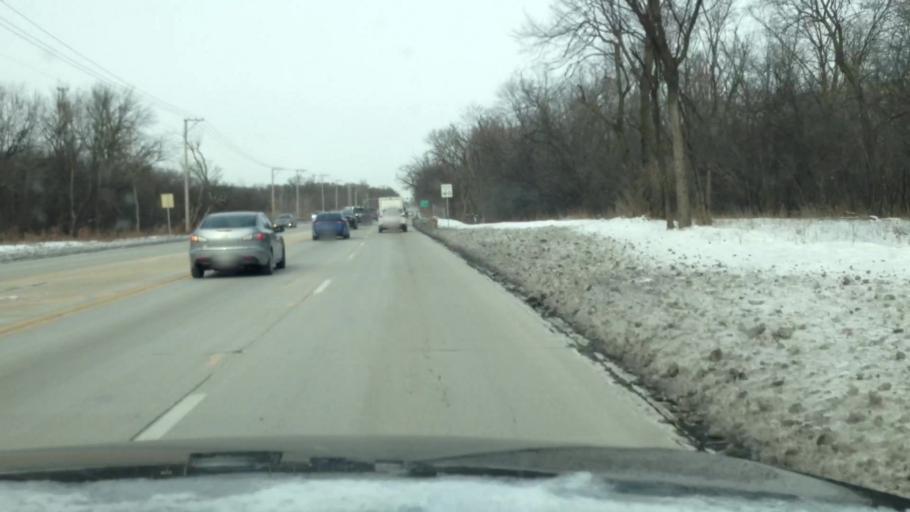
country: US
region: Illinois
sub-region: Cook County
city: River Grove
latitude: 41.9129
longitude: -87.8366
